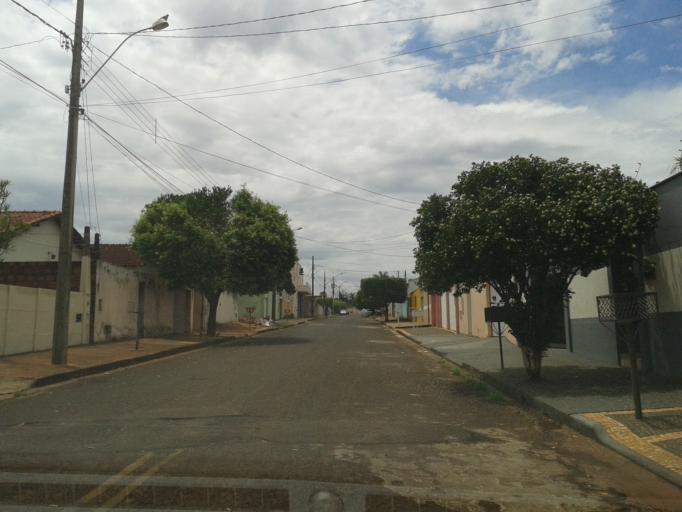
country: BR
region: Minas Gerais
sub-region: Ituiutaba
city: Ituiutaba
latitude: -18.9915
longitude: -49.4630
